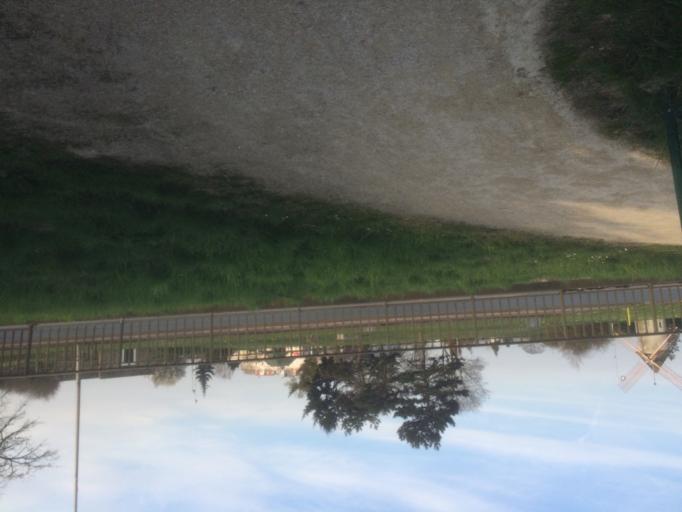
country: FR
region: Ile-de-France
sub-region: Departement de l'Essonne
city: Morsang-sur-Orge
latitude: 48.6615
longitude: 2.3737
